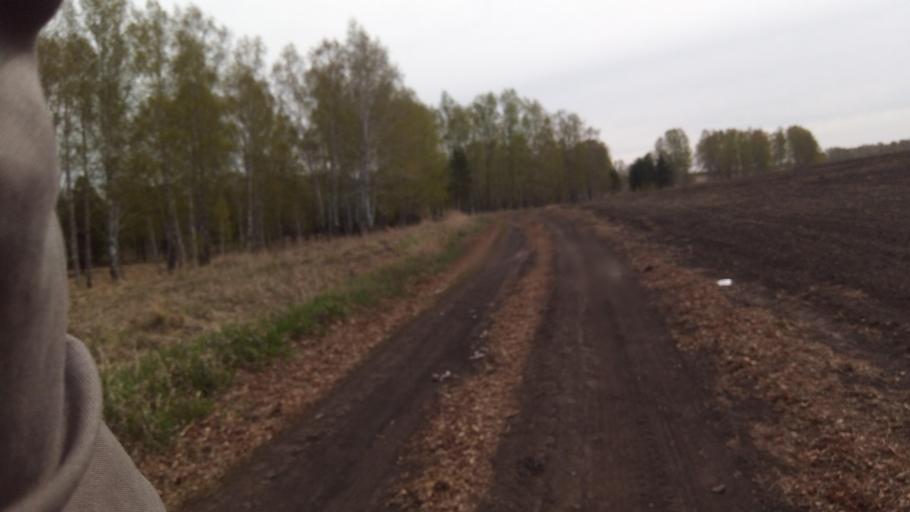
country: RU
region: Chelyabinsk
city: Timiryazevskiy
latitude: 55.0186
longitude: 60.8547
